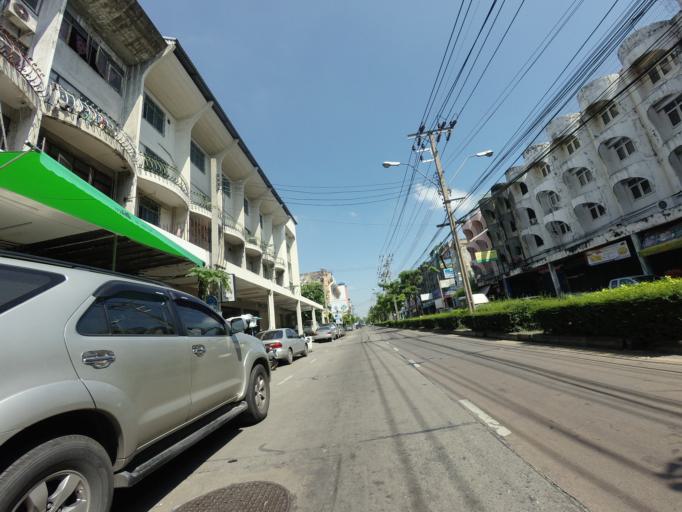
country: TH
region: Bangkok
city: Bang Kapi
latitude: 13.7715
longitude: 100.6415
